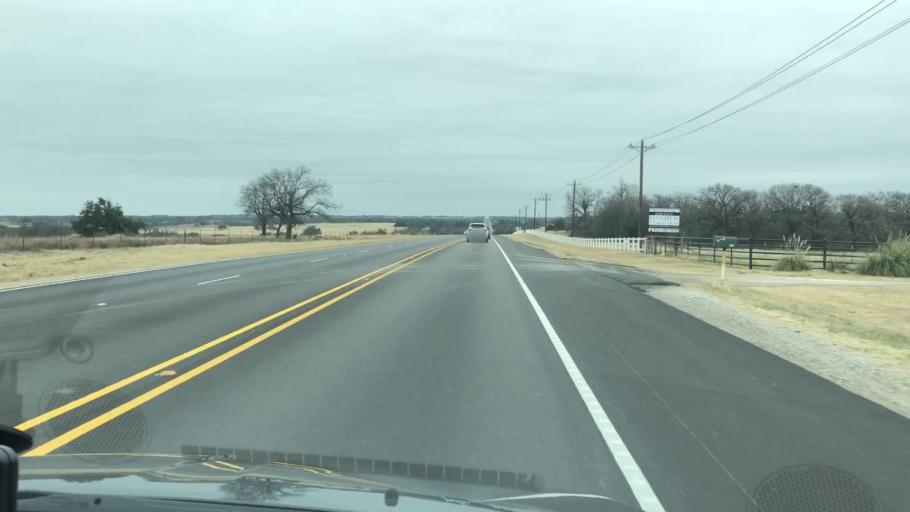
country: US
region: Texas
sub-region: Erath County
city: Stephenville
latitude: 32.2951
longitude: -98.1894
